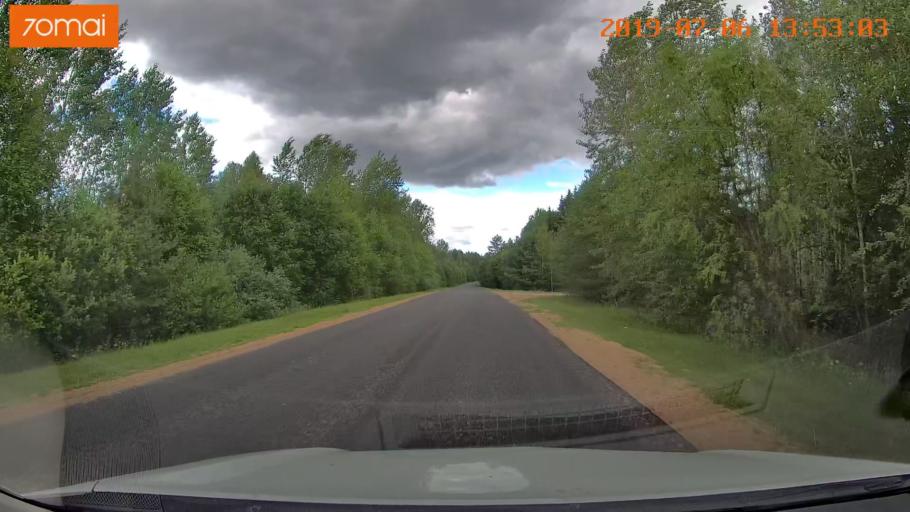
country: BY
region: Minsk
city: Ivyanyets
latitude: 53.7288
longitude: 26.8264
